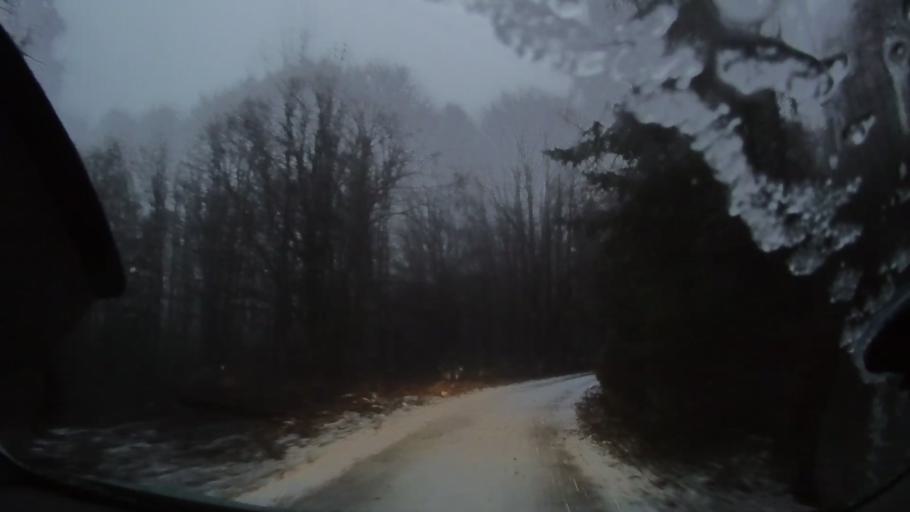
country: RO
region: Alba
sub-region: Comuna Avram Iancu
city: Avram Iancu
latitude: 46.3105
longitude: 22.8003
